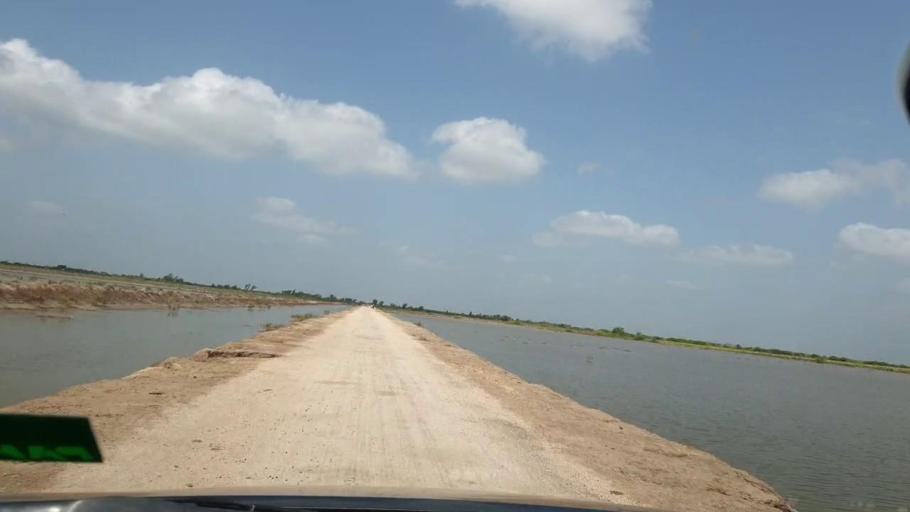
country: PK
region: Sindh
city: Kadhan
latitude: 24.5956
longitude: 69.1302
